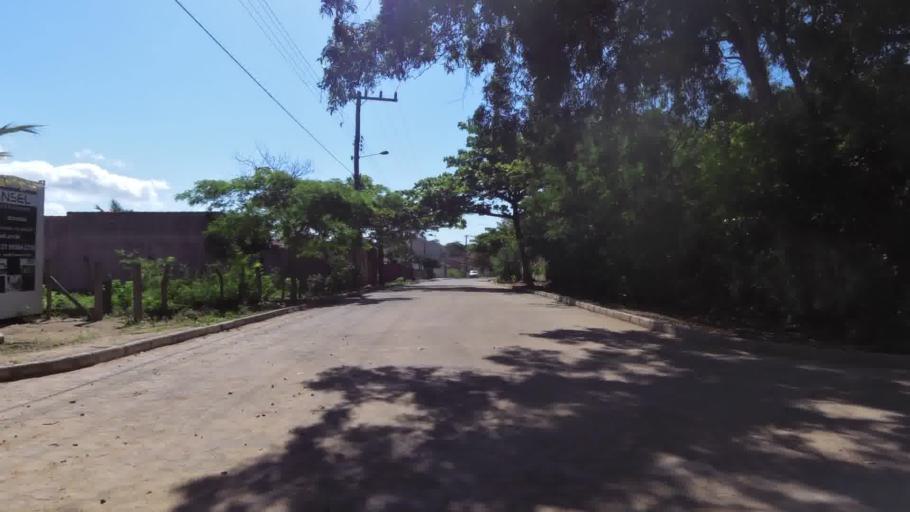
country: BR
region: Espirito Santo
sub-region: Piuma
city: Piuma
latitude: -20.8367
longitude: -40.6286
